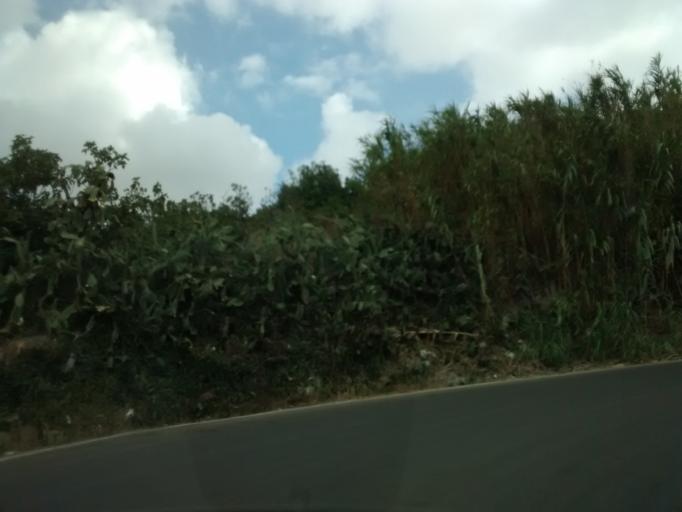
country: ES
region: Andalusia
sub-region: Provincia de Cadiz
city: Medina Sidonia
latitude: 36.4590
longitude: -5.9324
